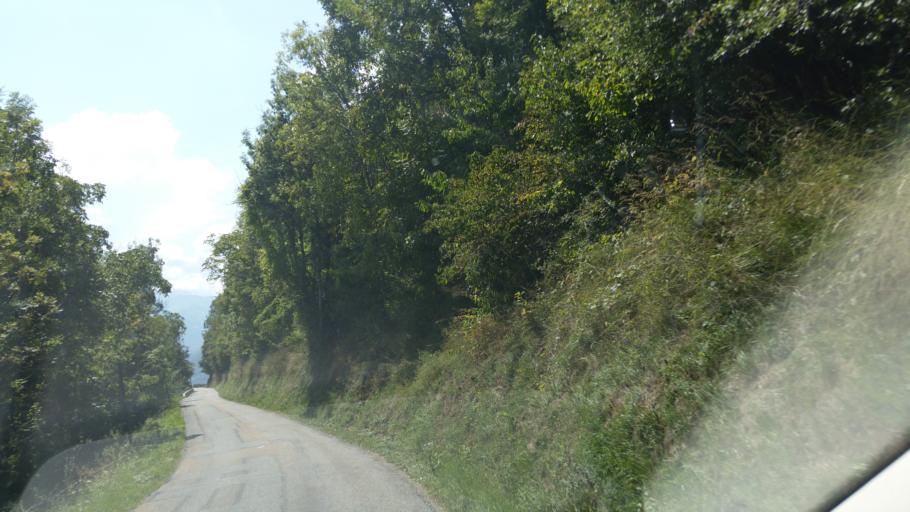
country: FR
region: Rhone-Alpes
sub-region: Departement de la Savoie
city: La Chambre
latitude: 45.3853
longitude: 6.3149
